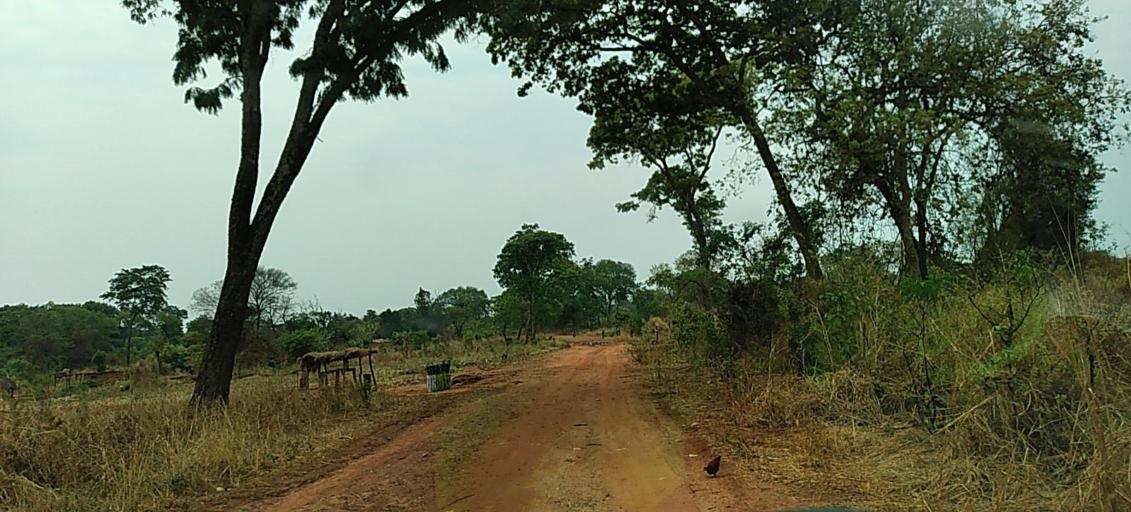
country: ZM
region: North-Western
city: Solwezi
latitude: -12.3388
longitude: 26.5249
